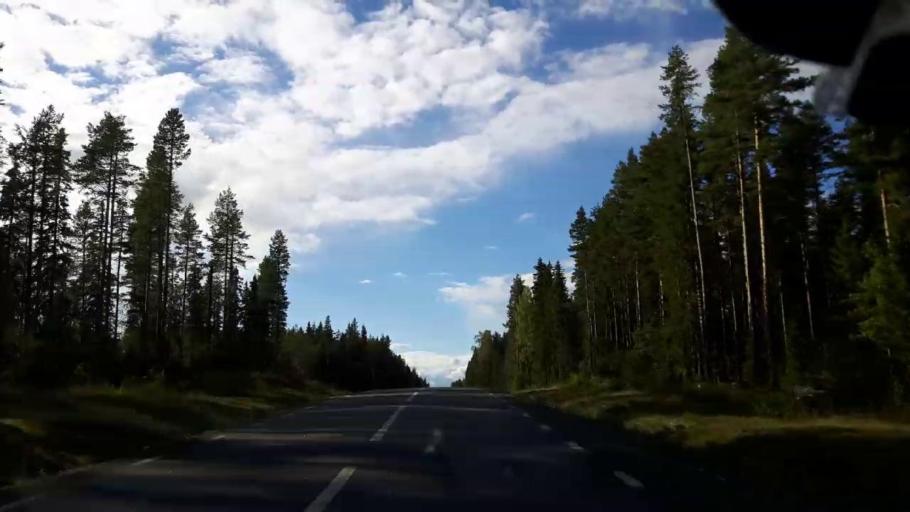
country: SE
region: Jaemtland
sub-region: Stroemsunds Kommun
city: Stroemsund
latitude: 63.5633
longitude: 15.7969
